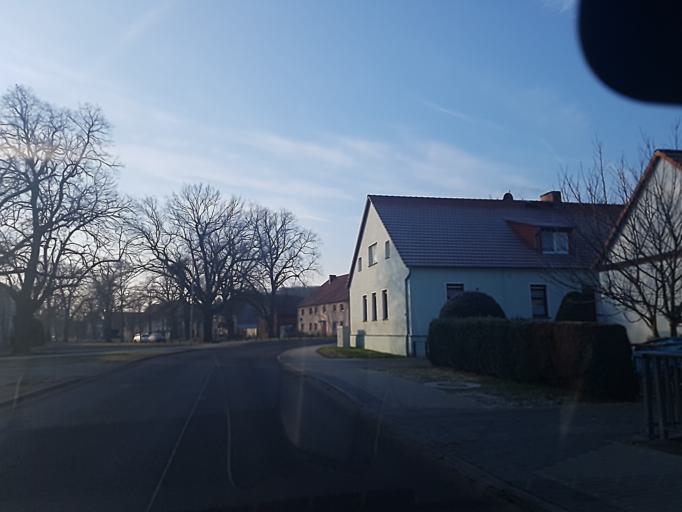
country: DE
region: Brandenburg
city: Golzow
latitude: 52.2416
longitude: 12.5816
